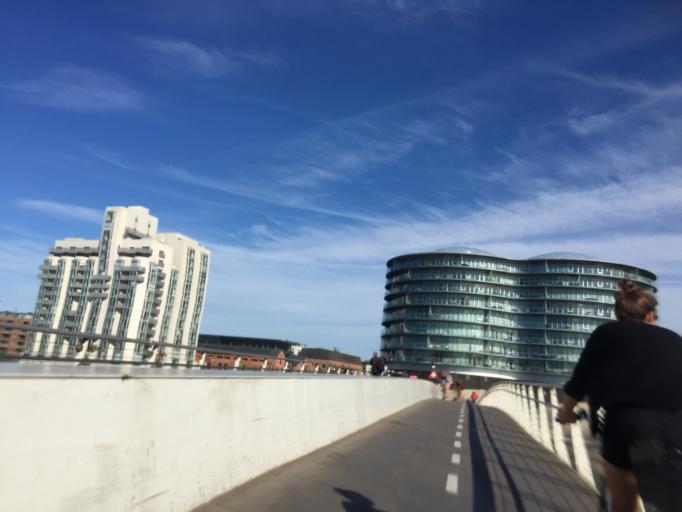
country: DK
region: Capital Region
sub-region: Kobenhavn
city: Copenhagen
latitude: 55.6616
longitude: 12.5662
